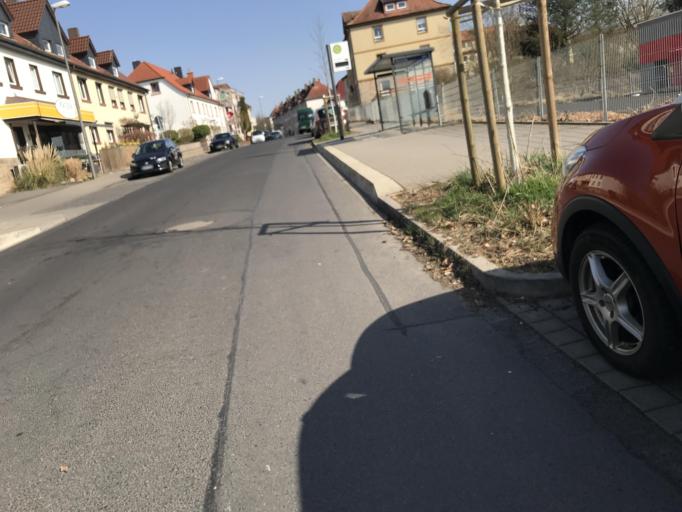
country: DE
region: Hesse
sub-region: Regierungsbezirk Kassel
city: Fulda
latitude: 50.5380
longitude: 9.6767
